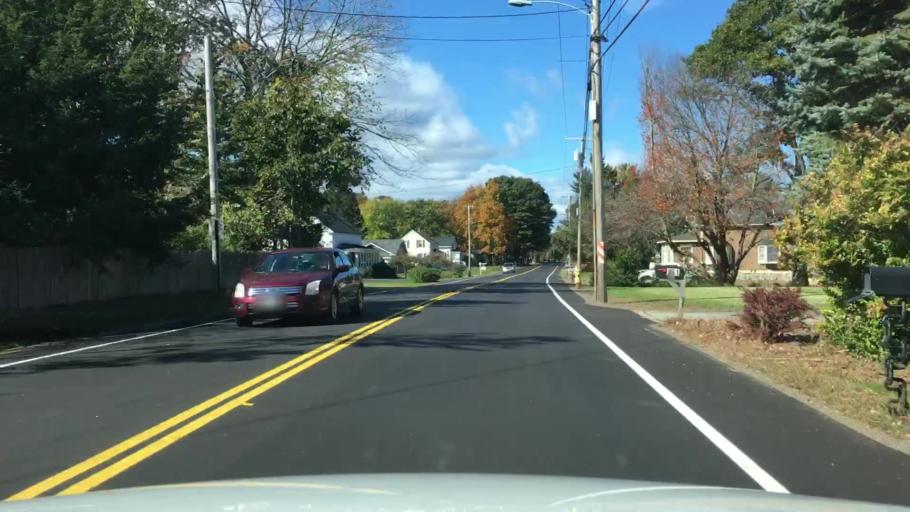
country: US
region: Maine
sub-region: York County
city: Biddeford
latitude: 43.4670
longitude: -70.4448
